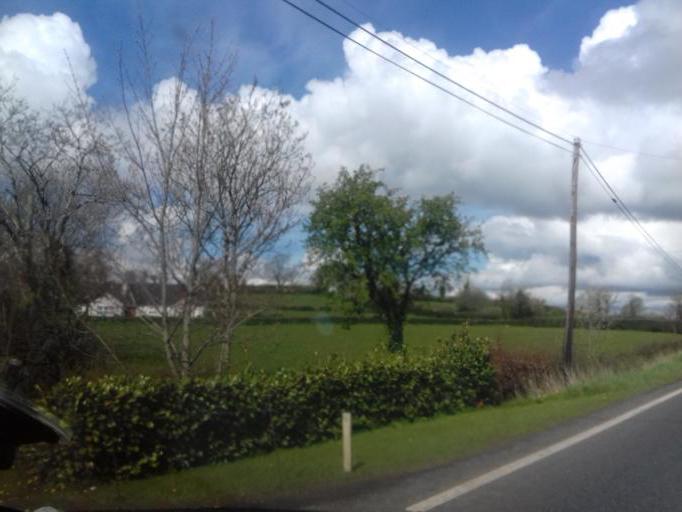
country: IE
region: Ulster
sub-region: An Cabhan
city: Ballyconnell
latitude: 54.1423
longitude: -7.5127
